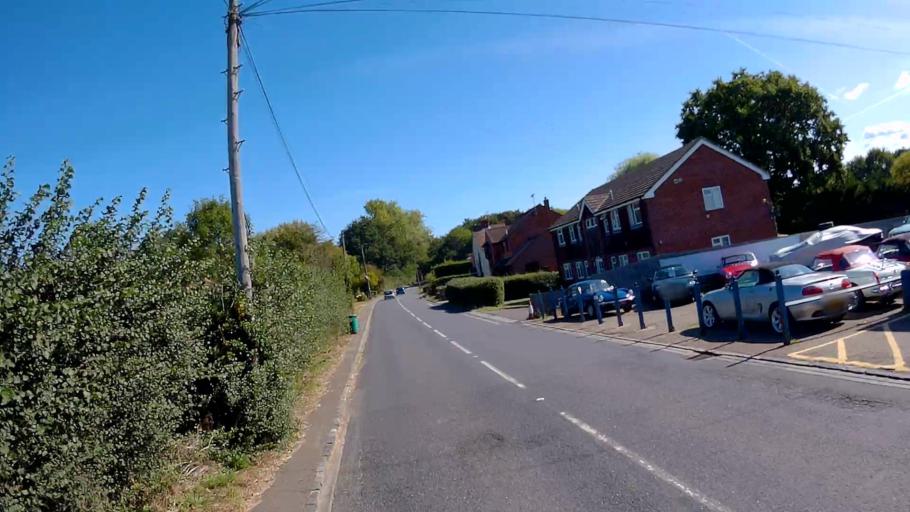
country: GB
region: England
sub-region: West Berkshire
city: Stratfield Mortimer
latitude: 51.3709
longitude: -1.0070
